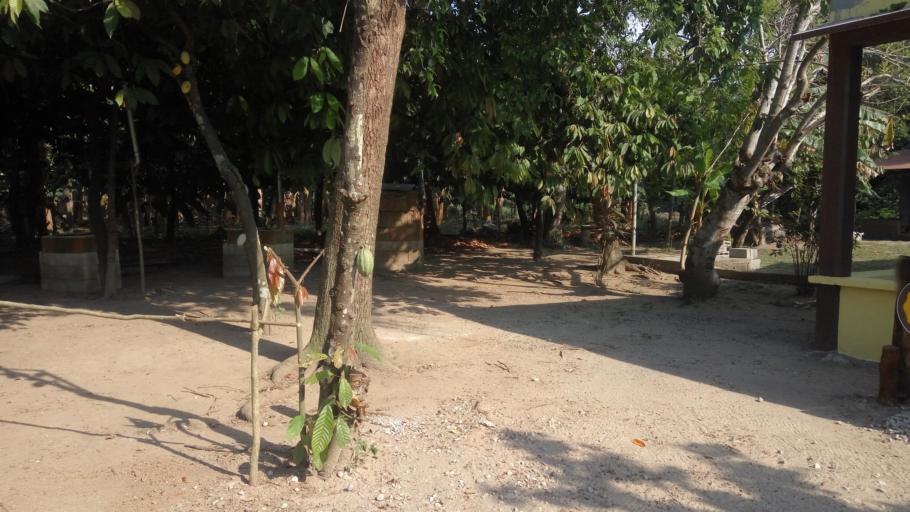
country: MX
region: Tabasco
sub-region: Cunduacan
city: Cumuapa 1ra. Seccion
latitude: 17.9773
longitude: -93.1323
